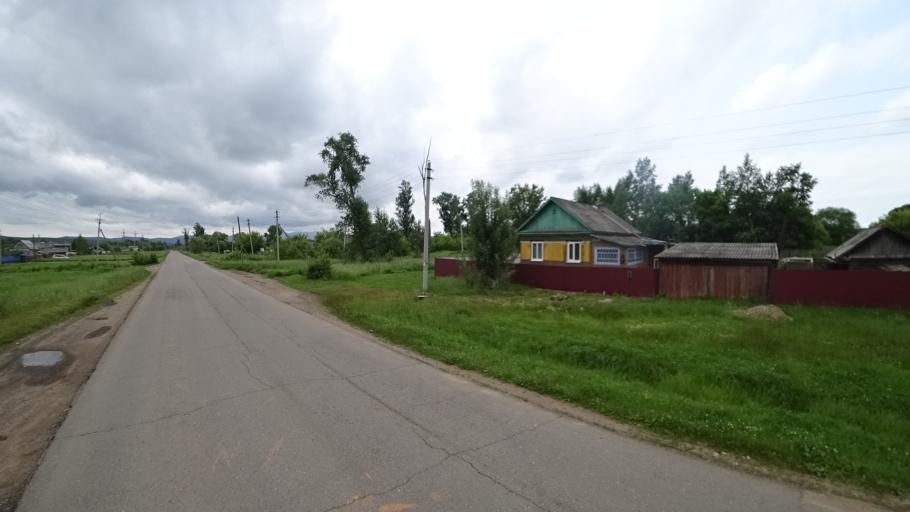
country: RU
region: Primorskiy
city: Novosysoyevka
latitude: 44.2378
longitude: 133.3693
